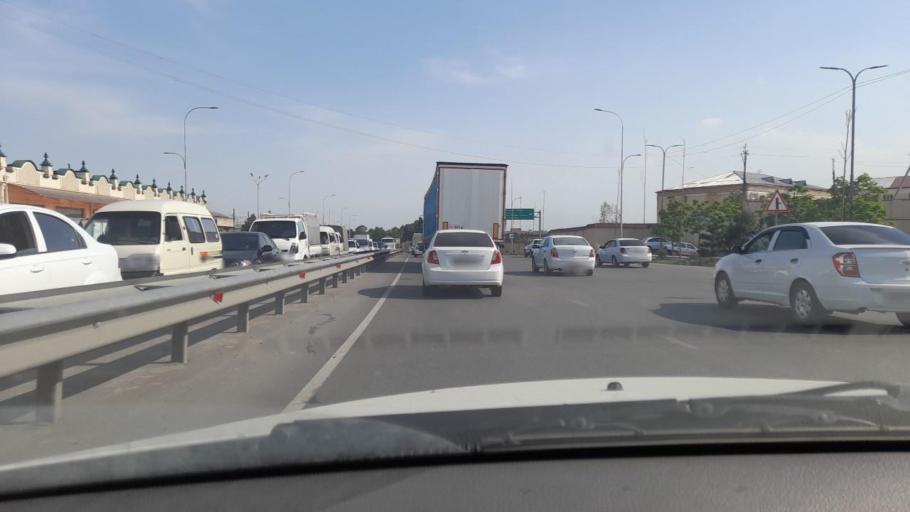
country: UZ
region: Samarqand
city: Samarqand
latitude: 39.6804
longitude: 67.0045
